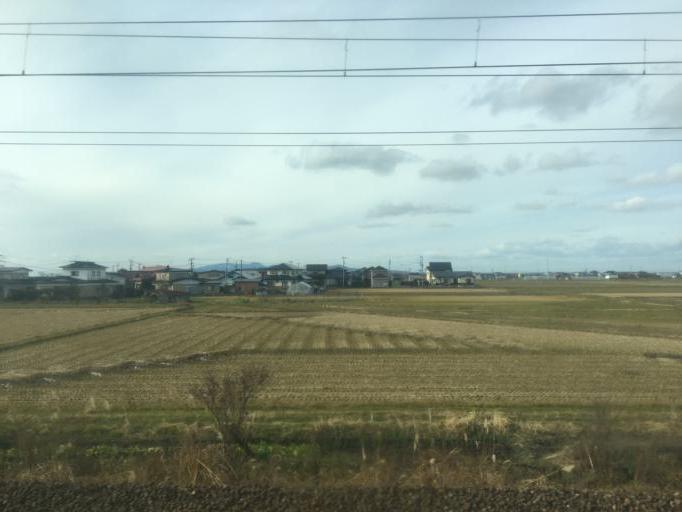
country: JP
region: Akita
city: Tenno
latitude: 39.9179
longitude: 140.0768
